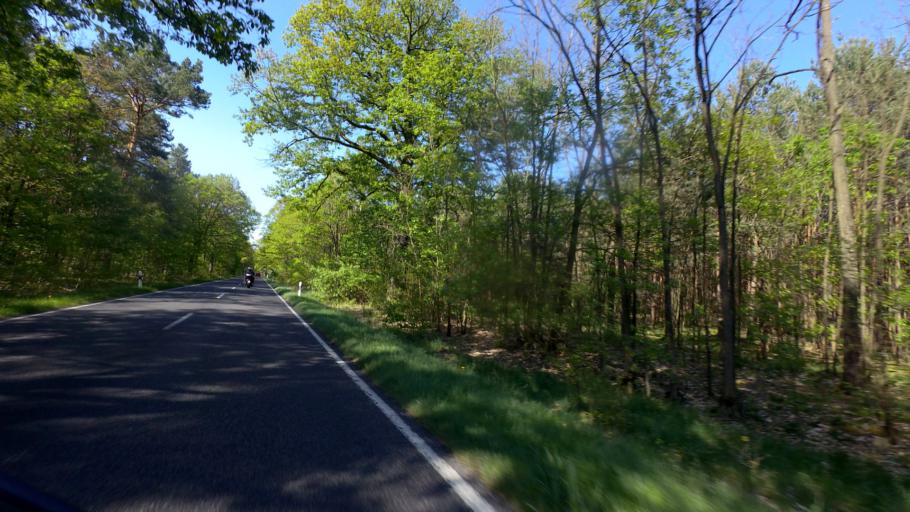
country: DE
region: Brandenburg
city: Bestensee
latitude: 52.2168
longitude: 13.6867
